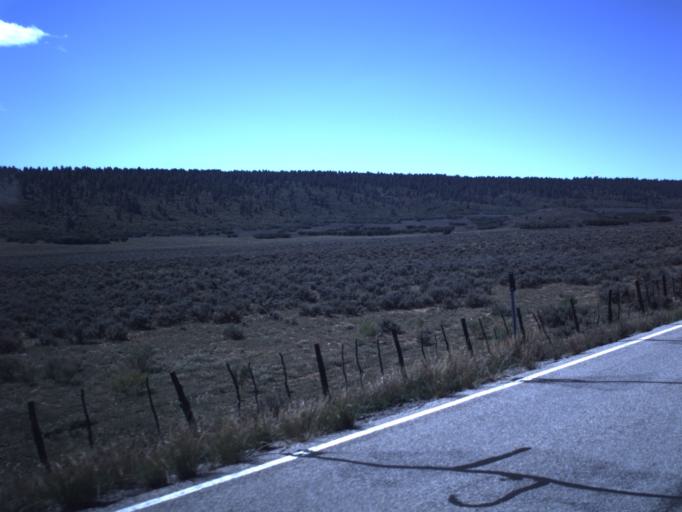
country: US
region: Utah
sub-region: Grand County
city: Moab
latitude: 38.3290
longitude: -109.1394
